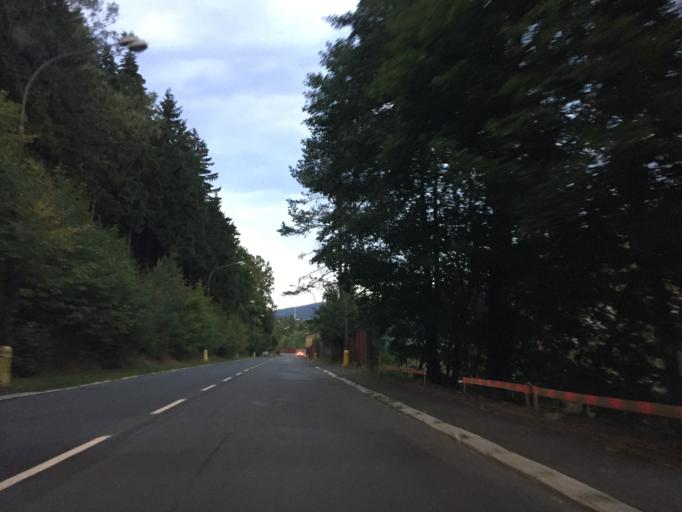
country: CZ
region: Liberecky
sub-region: Okres Jablonec nad Nisou
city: Jablonec nad Nisou
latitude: 50.7113
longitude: 15.1753
